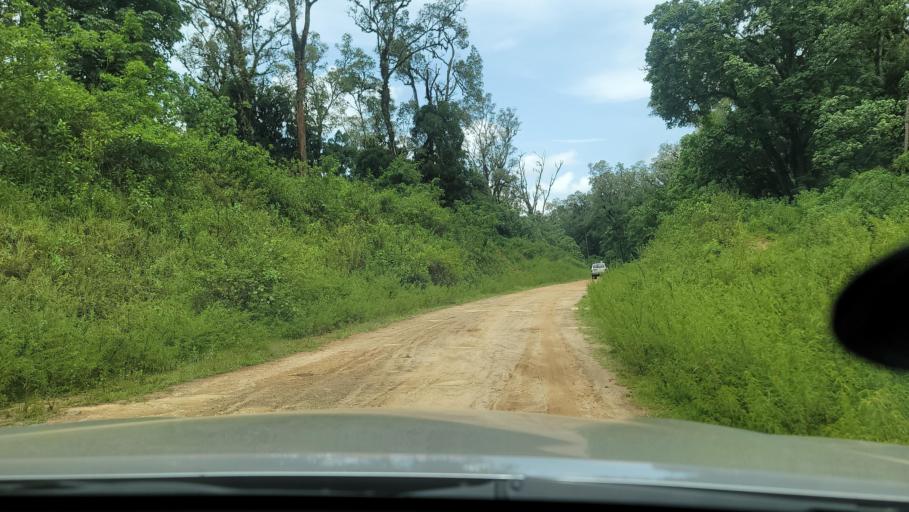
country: ET
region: Southern Nations, Nationalities, and People's Region
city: Bonga
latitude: 7.6573
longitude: 36.2480
